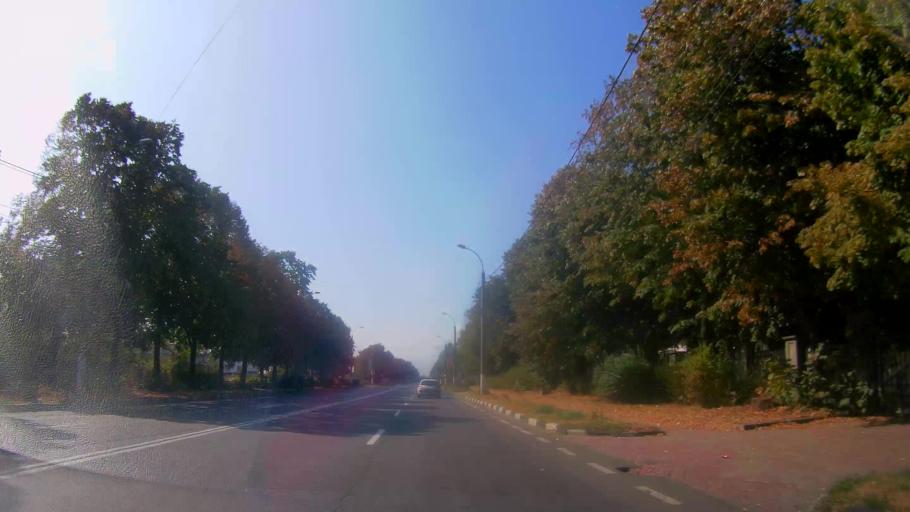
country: RO
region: Giurgiu
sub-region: Comuna Fratesti
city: Remus
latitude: 43.9301
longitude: 25.9756
